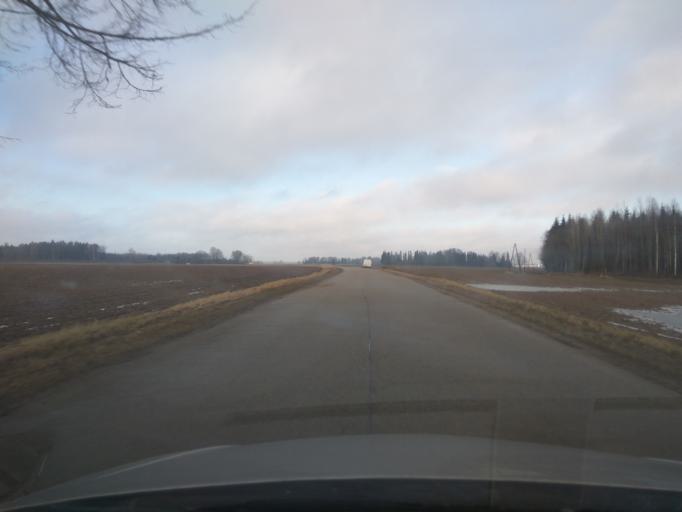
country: LV
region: Saldus Rajons
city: Saldus
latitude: 56.7858
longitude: 22.3879
